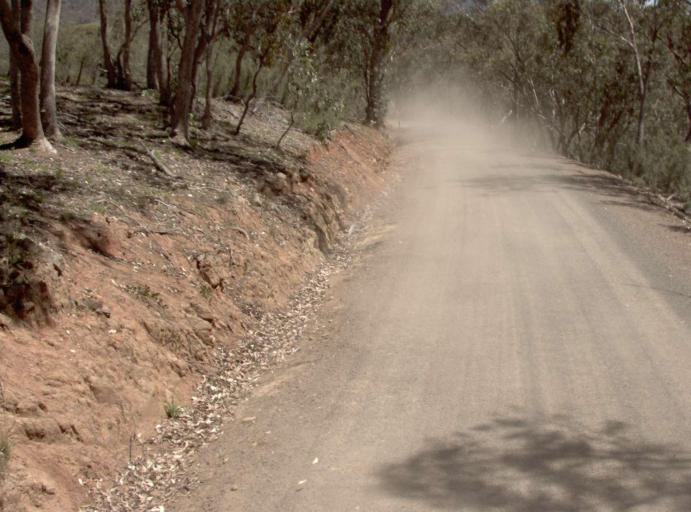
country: AU
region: New South Wales
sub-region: Snowy River
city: Jindabyne
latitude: -37.0799
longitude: 148.4516
